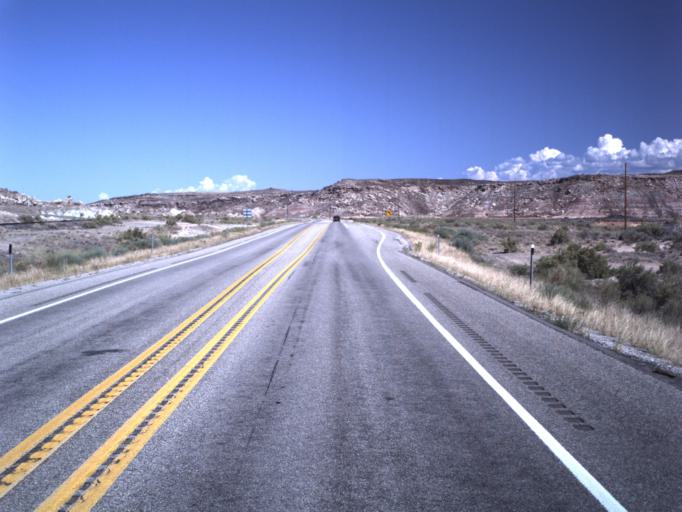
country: US
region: Utah
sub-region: Grand County
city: Moab
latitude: 38.7090
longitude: -109.7028
